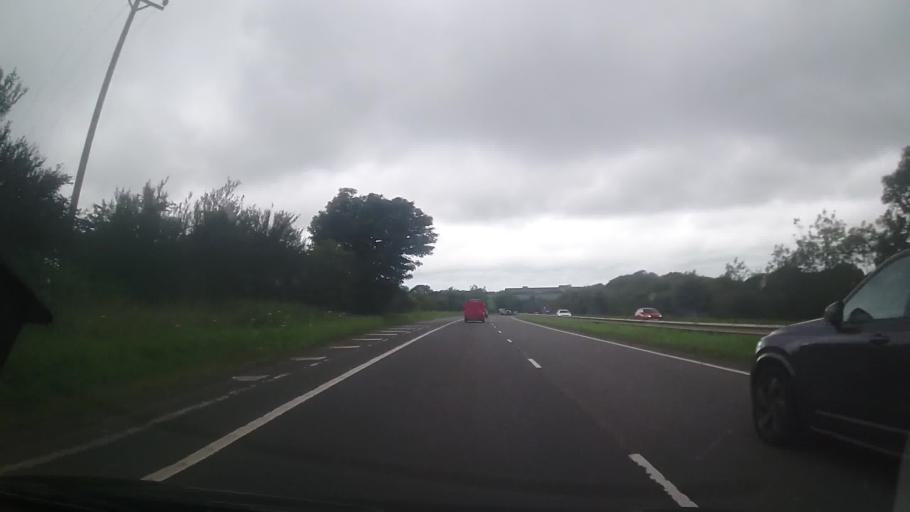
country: GB
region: Wales
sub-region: Gwynedd
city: Bangor
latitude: 53.2026
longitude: -4.1421
